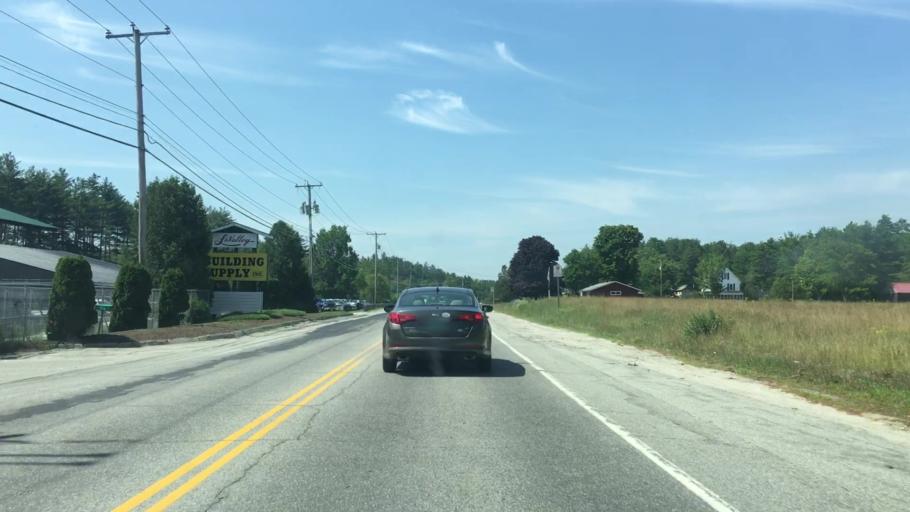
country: US
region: New Hampshire
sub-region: Sullivan County
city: Newport
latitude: 43.3770
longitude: -72.1551
